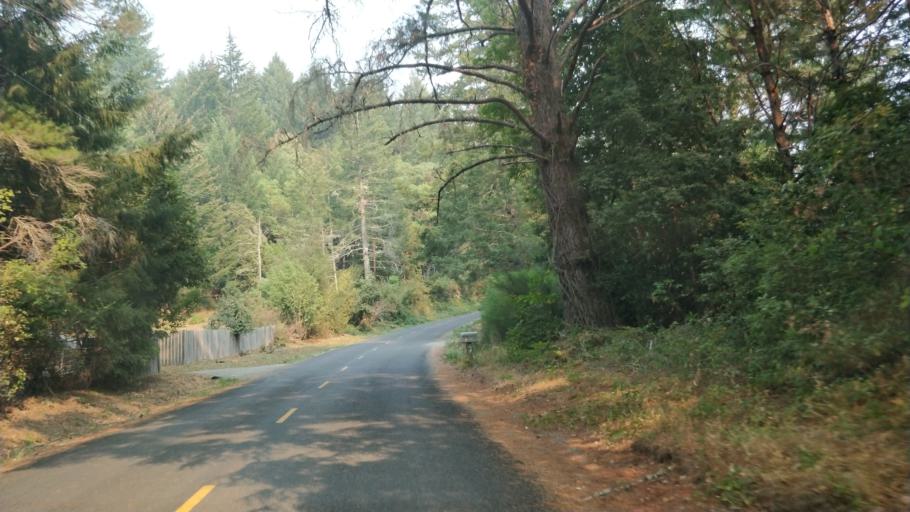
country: US
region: California
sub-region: Humboldt County
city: Rio Dell
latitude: 40.2699
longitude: -124.2153
